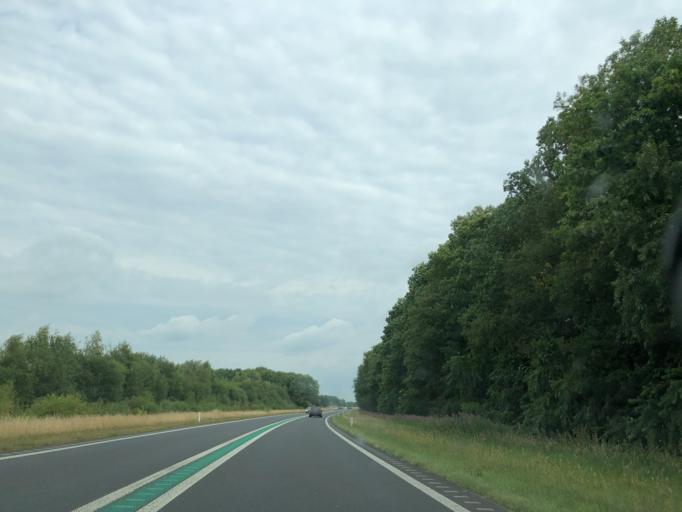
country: NL
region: Drenthe
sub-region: Gemeente Tynaarlo
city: Zuidlaren
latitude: 53.0789
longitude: 6.6737
